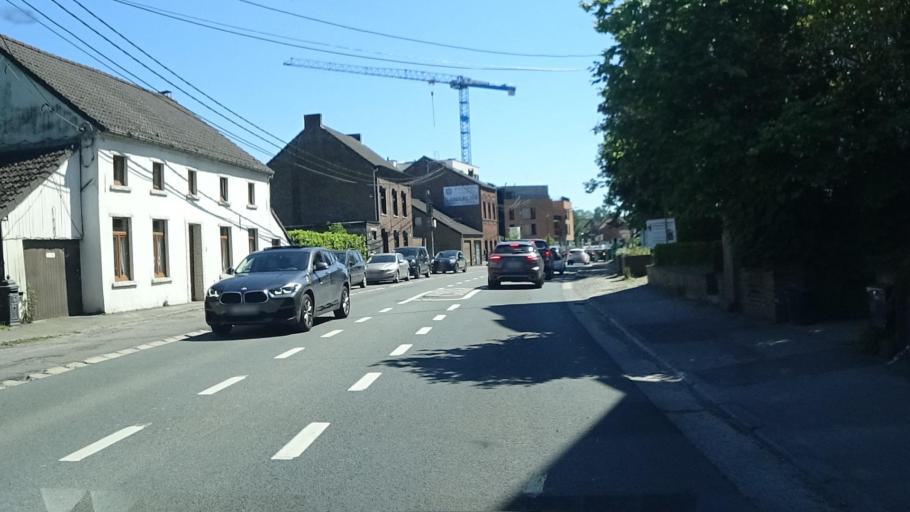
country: BE
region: Wallonia
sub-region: Province du Brabant Wallon
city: Ottignies
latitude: 50.6510
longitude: 4.5639
